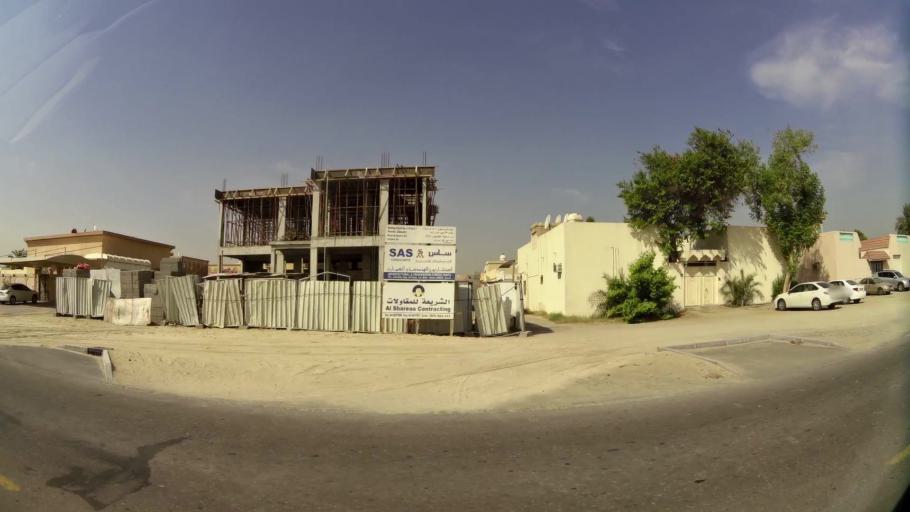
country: AE
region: Ash Shariqah
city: Sharjah
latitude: 25.2642
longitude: 55.3959
